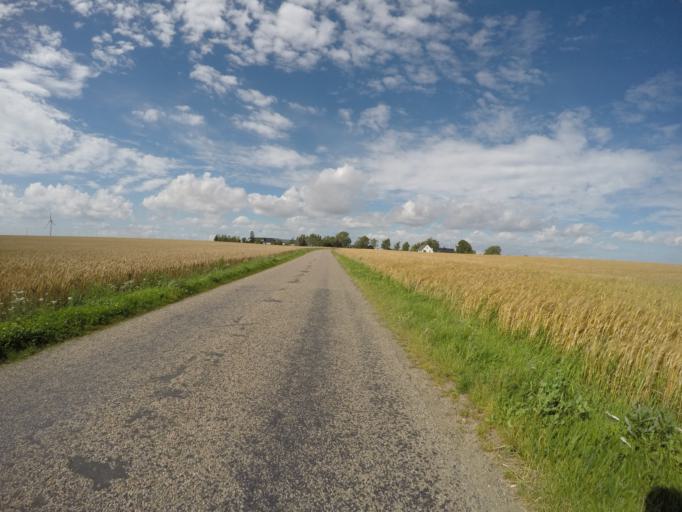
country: SE
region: Skane
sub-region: Simrishamns Kommun
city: Simrishamn
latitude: 55.4793
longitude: 14.1667
